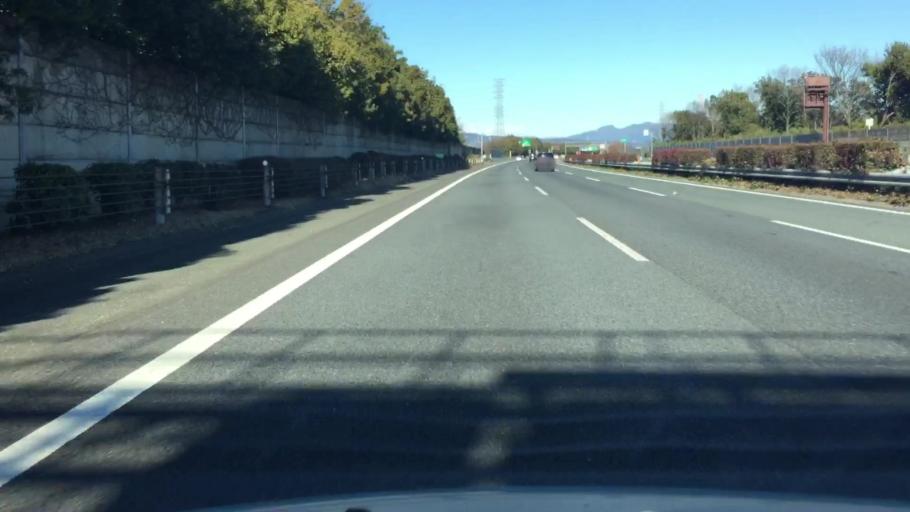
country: JP
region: Gunma
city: Takasaki
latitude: 36.3643
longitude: 139.0325
